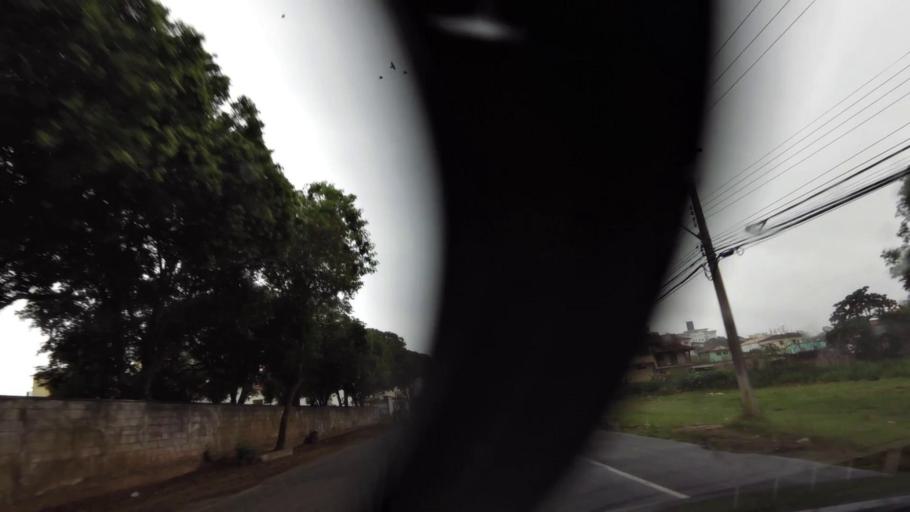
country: BR
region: Espirito Santo
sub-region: Guarapari
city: Guarapari
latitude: -20.7358
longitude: -40.5399
